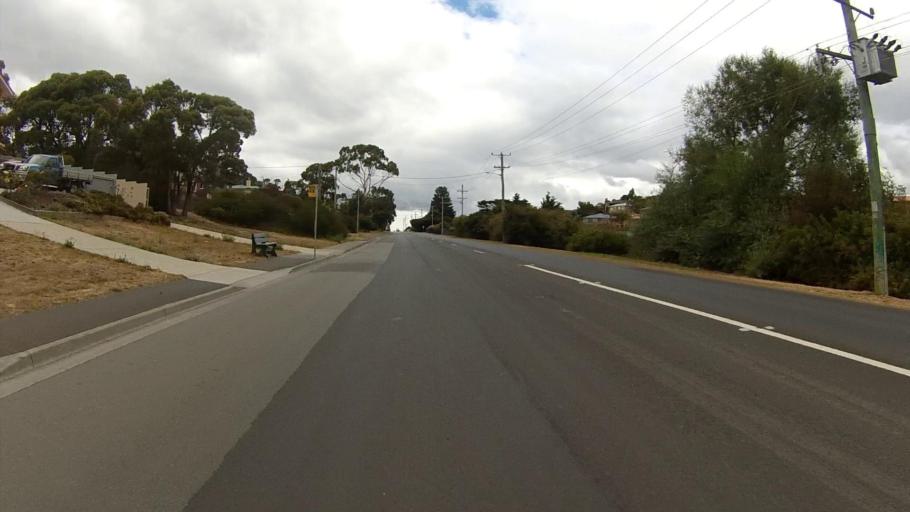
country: AU
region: Tasmania
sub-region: Glenorchy
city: Austins Ferry
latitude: -42.7670
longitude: 147.2439
